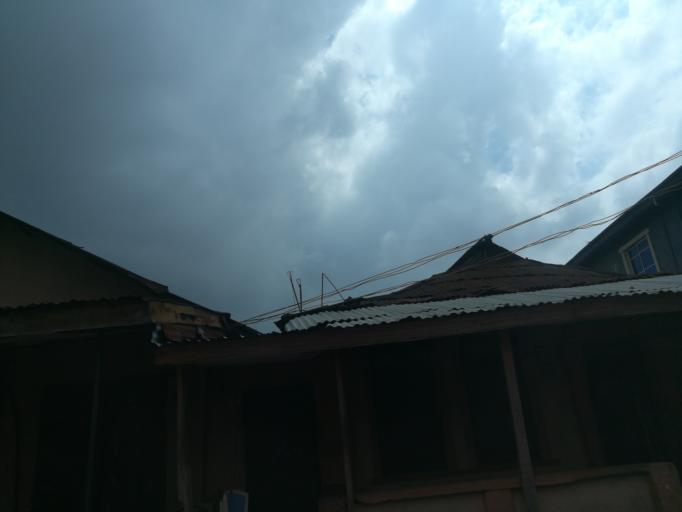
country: NG
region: Lagos
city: Mushin
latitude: 6.5292
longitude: 3.3640
